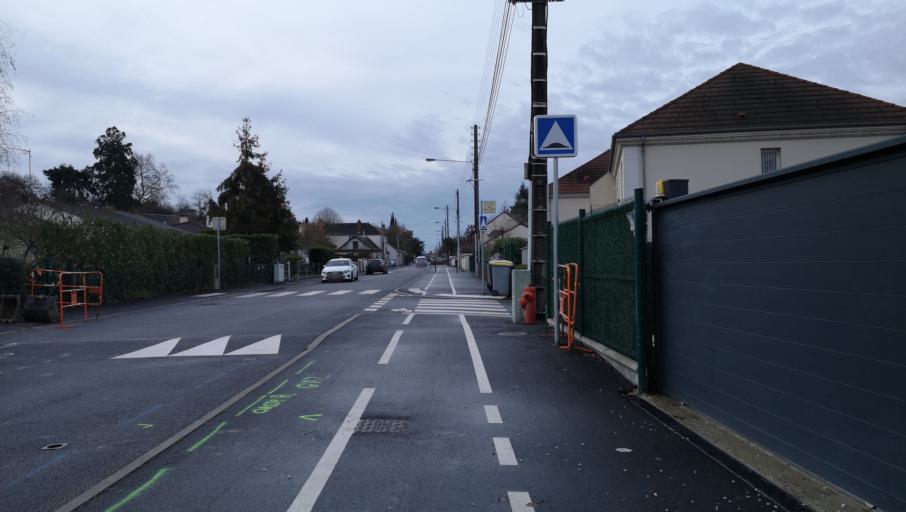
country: FR
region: Centre
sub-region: Departement du Loiret
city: Saint-Jean-de-Braye
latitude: 47.9143
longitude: 1.9571
